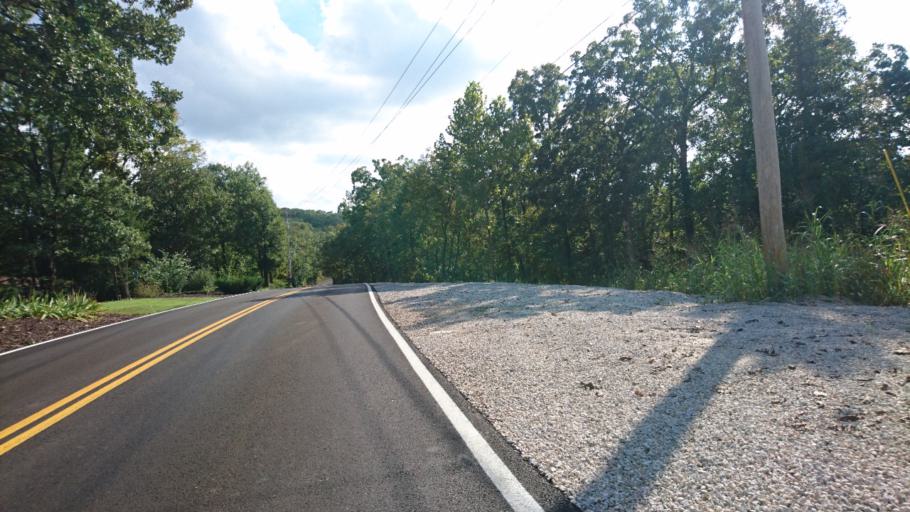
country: US
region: Missouri
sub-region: Saint Louis County
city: Eureka
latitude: 38.5341
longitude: -90.6400
